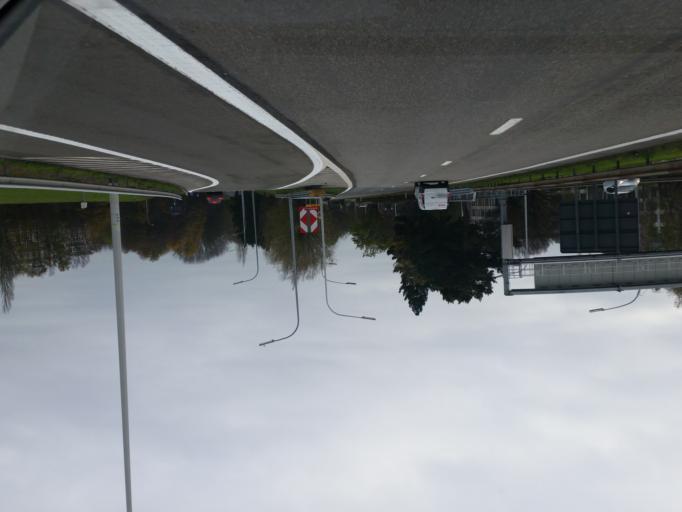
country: BE
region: Flanders
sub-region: Provincie Vlaams-Brabant
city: Diegem
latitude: 50.8852
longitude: 4.4491
